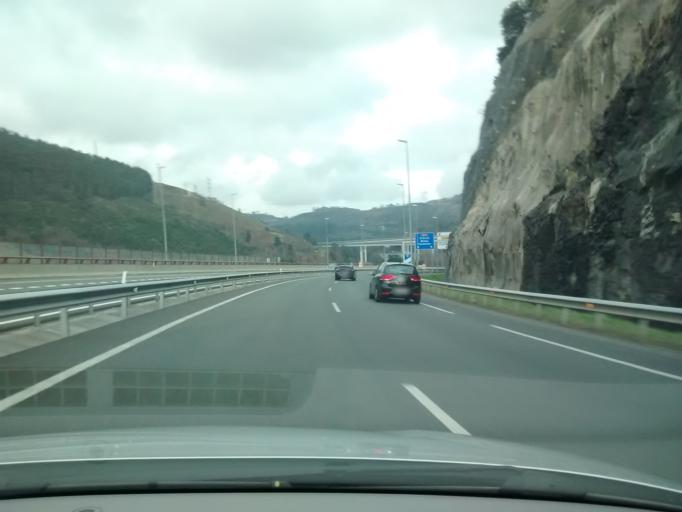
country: ES
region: Basque Country
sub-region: Bizkaia
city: Alonsotegi
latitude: 43.2445
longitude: -2.9860
